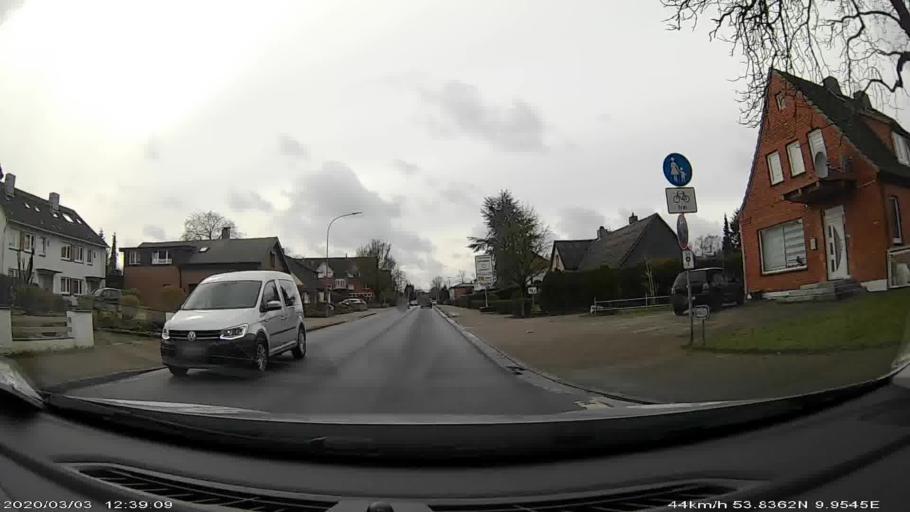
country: DE
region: Schleswig-Holstein
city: Kaltenkirchen
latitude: 53.8354
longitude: 9.9534
